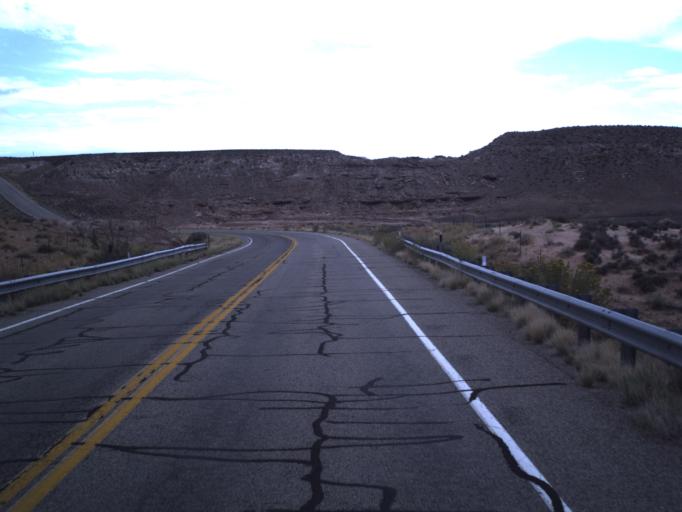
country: US
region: Utah
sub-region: San Juan County
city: Blanding
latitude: 37.2841
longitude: -109.3850
